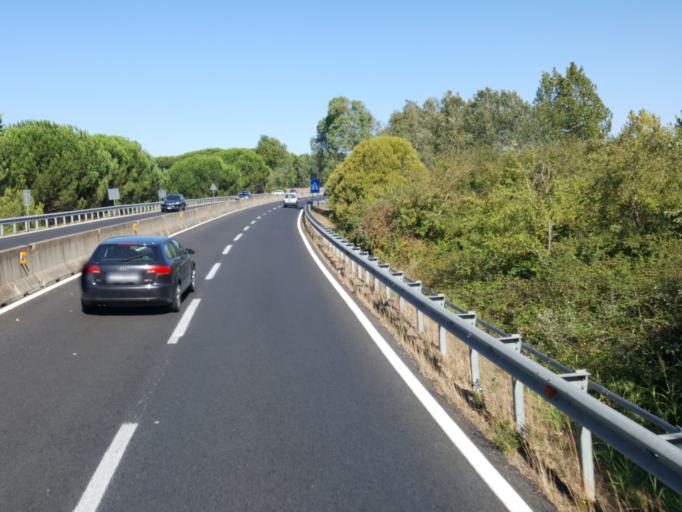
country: IT
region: Tuscany
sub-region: Provincia di Grosseto
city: Albinia
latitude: 42.4803
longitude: 11.2224
